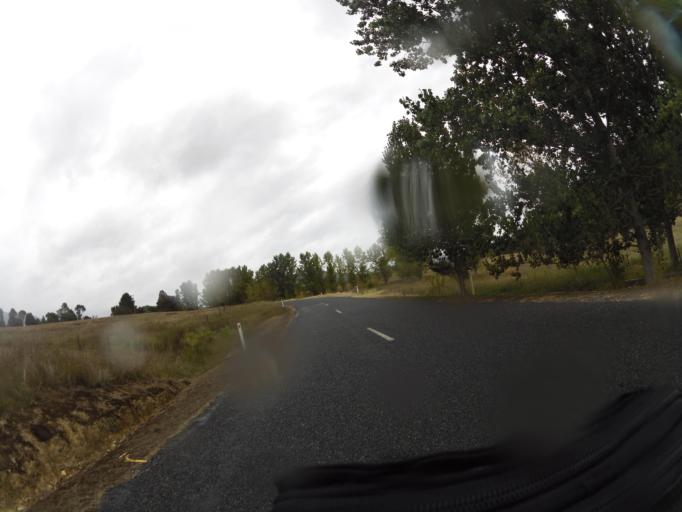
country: AU
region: New South Wales
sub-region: Greater Hume Shire
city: Holbrook
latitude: -36.2323
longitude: 147.6523
